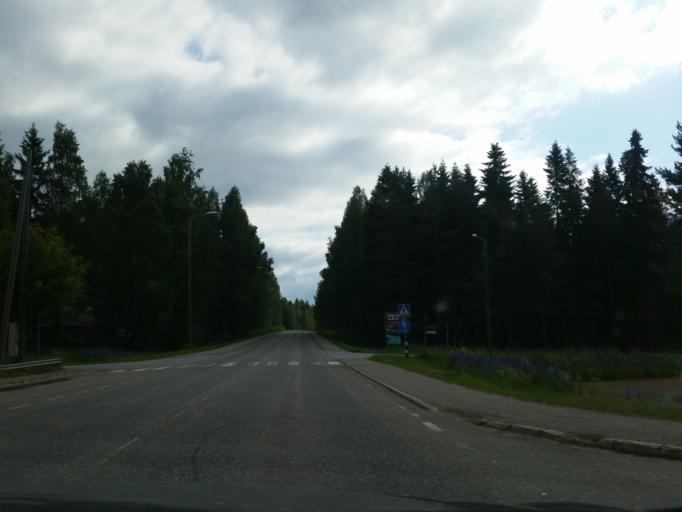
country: FI
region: Northern Savo
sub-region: Sisae-Savo
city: Tervo
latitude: 62.9562
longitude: 26.7595
